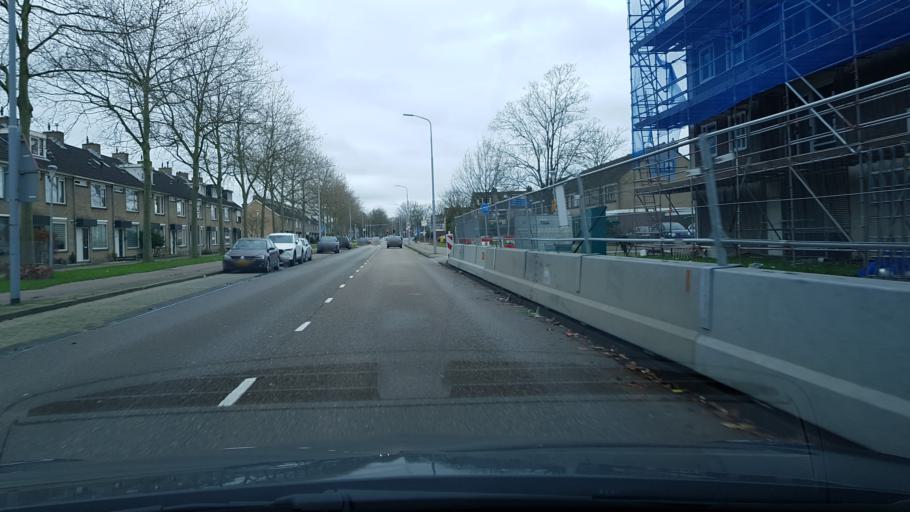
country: NL
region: North Holland
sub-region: Gemeente Haarlemmermeer
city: Hoofddorp
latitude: 52.2984
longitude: 4.6887
